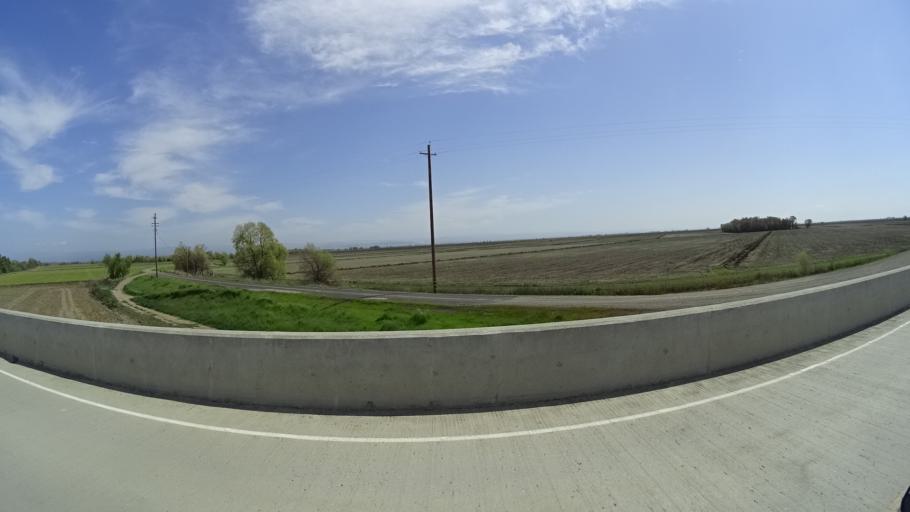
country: US
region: California
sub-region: Butte County
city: Durham
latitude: 39.5321
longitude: -121.8566
